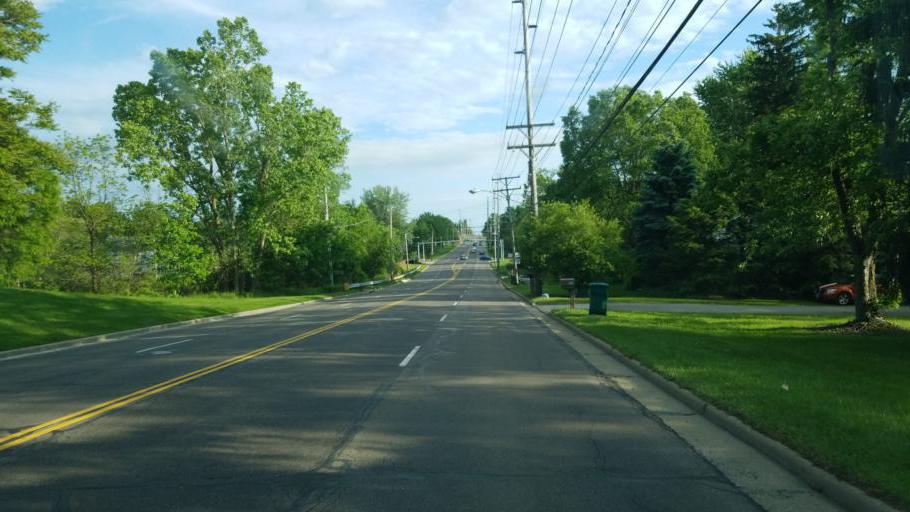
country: US
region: Ohio
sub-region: Summit County
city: Stow
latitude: 41.1965
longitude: -81.4405
